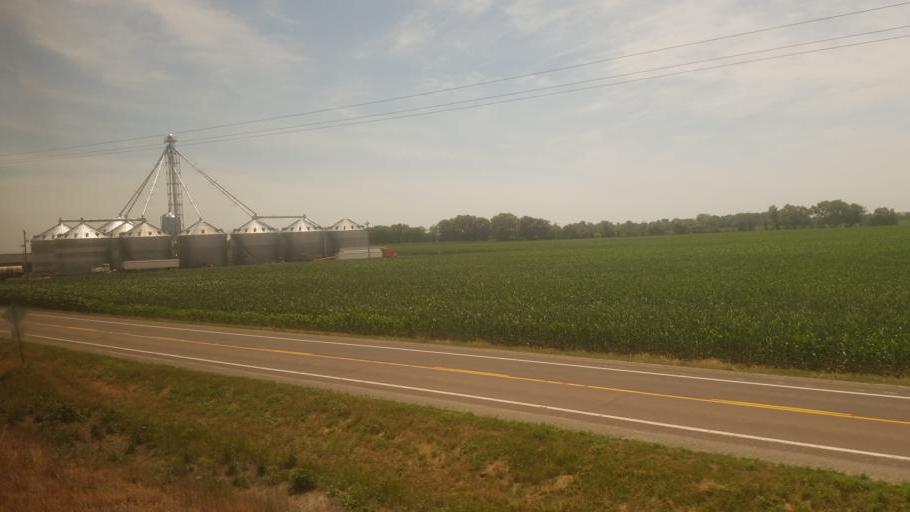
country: US
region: Missouri
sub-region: Carroll County
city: Carrollton
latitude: 39.3143
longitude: -93.6264
